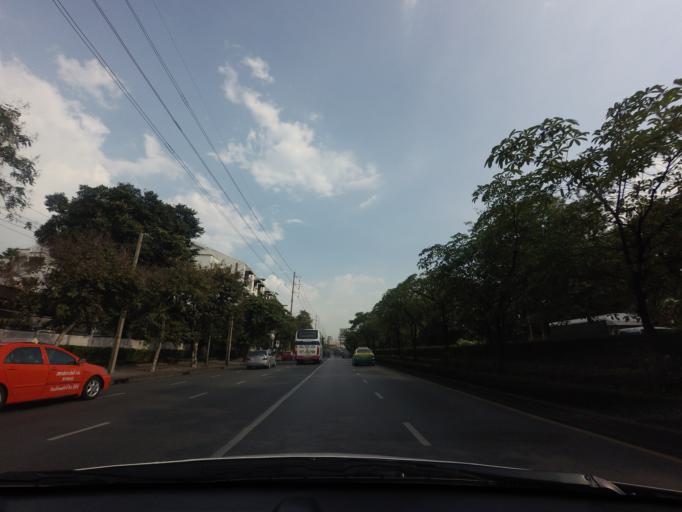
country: TH
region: Bangkok
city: Pom Prap Sattru Phai
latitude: 13.7600
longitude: 100.5176
